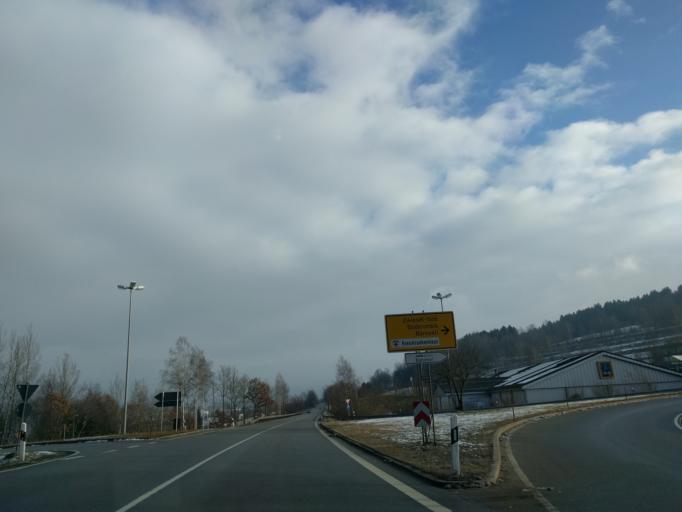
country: DE
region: Bavaria
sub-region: Lower Bavaria
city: Zwiesel
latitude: 49.0009
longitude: 13.2172
